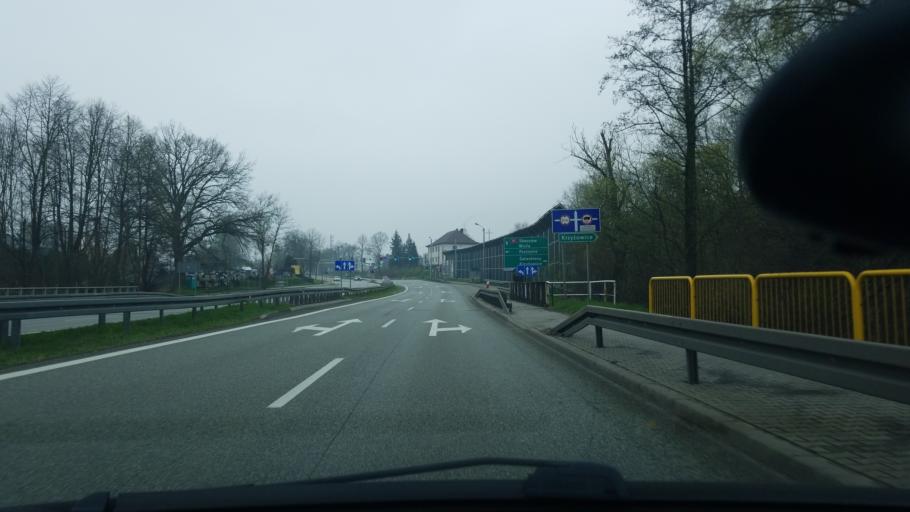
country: PL
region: Silesian Voivodeship
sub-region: Powiat pszczynski
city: Pawlowice
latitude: 49.9941
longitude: 18.7113
